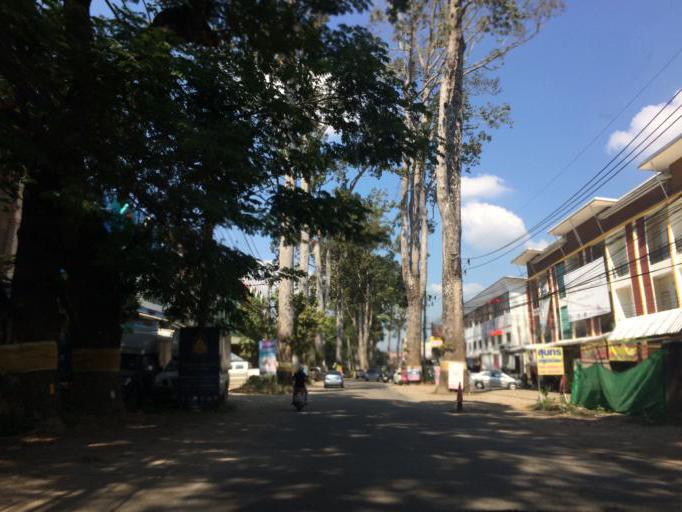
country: TH
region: Chiang Mai
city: Saraphi
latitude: 18.7408
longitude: 99.0142
